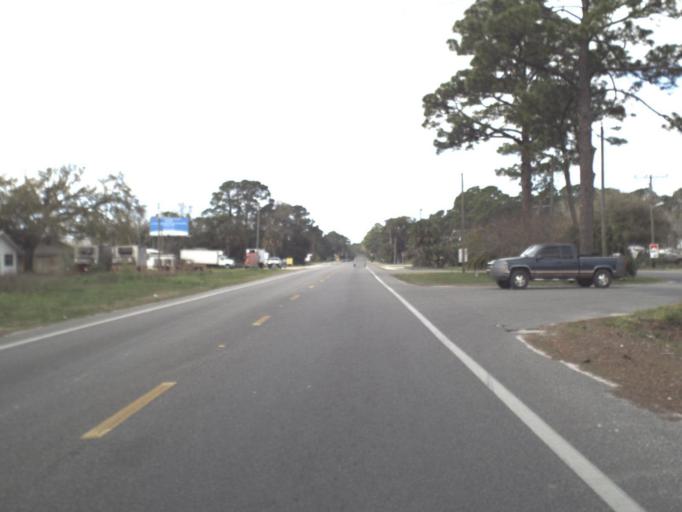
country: US
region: Florida
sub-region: Franklin County
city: Apalachicola
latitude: 29.7140
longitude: -85.0069
